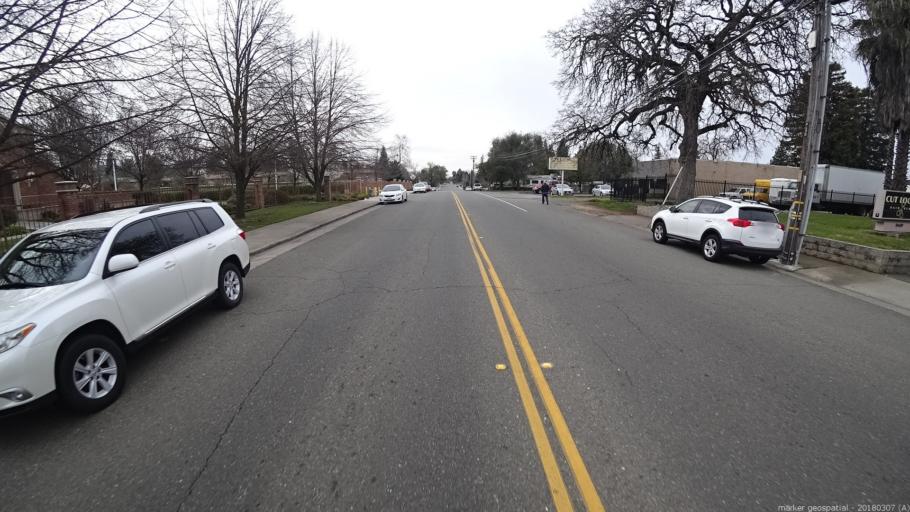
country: US
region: California
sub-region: Sacramento County
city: Carmichael
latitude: 38.6278
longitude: -121.3553
